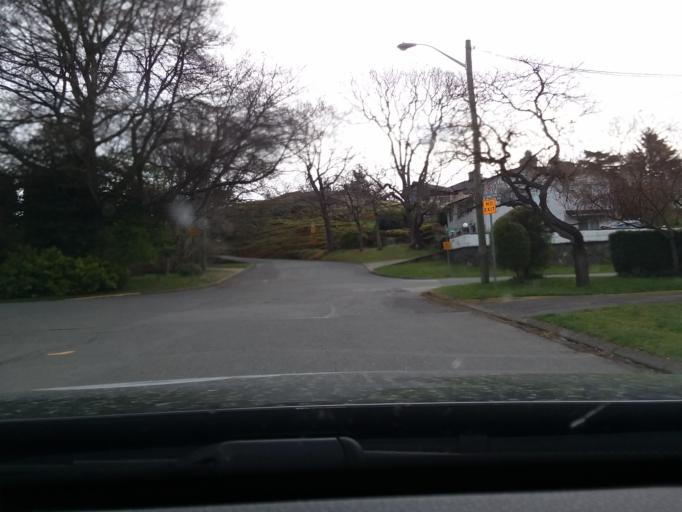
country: CA
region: British Columbia
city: Oak Bay
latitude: 48.4481
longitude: -123.3275
